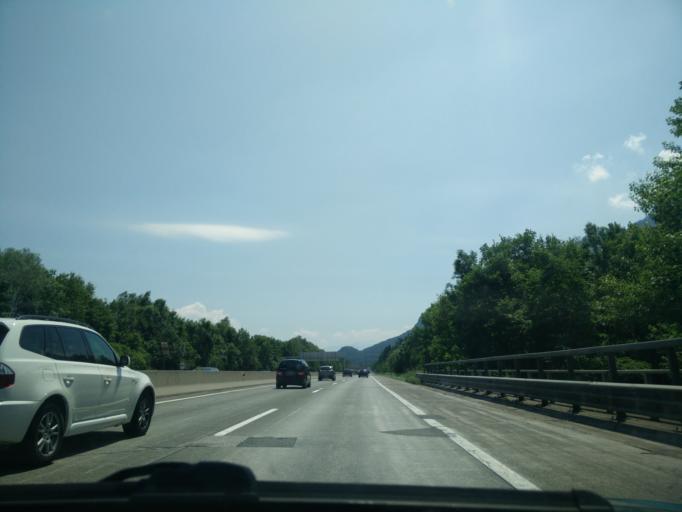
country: AT
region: Salzburg
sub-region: Politischer Bezirk Salzburg-Umgebung
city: Grodig
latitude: 47.7627
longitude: 12.9997
